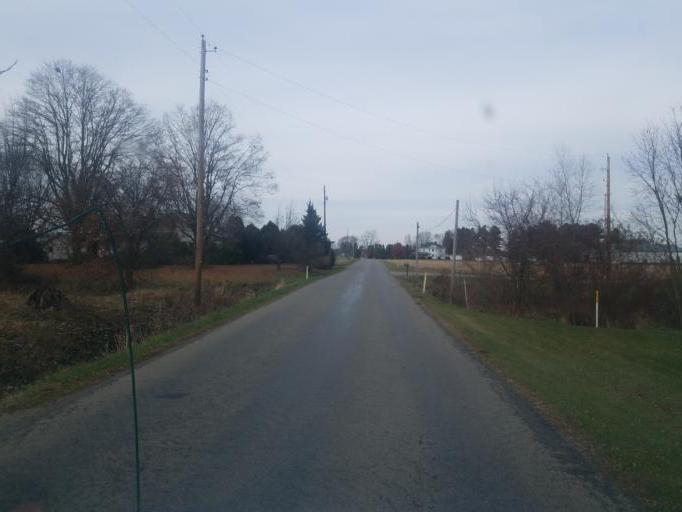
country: US
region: Ohio
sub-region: Knox County
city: Mount Vernon
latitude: 40.4006
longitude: -82.5126
